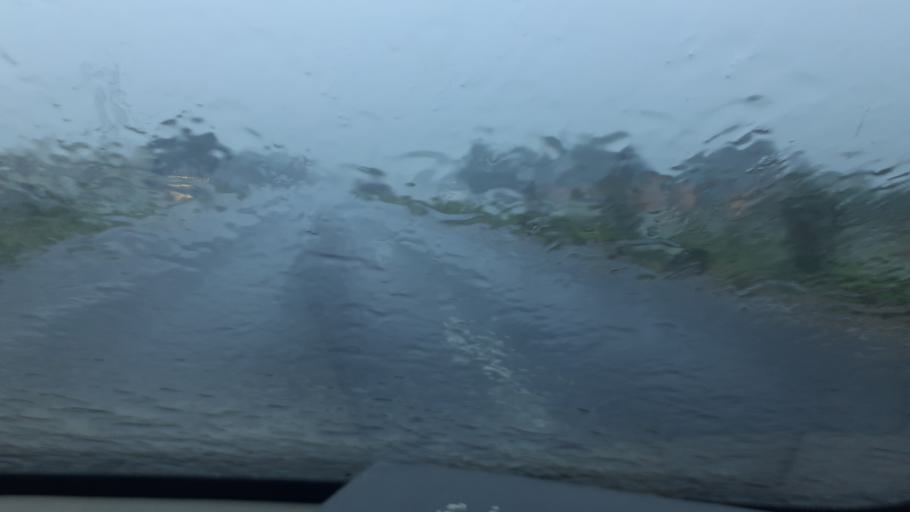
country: IN
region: Tamil Nadu
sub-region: Virudhunagar
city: Sattur
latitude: 9.4492
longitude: 77.9282
